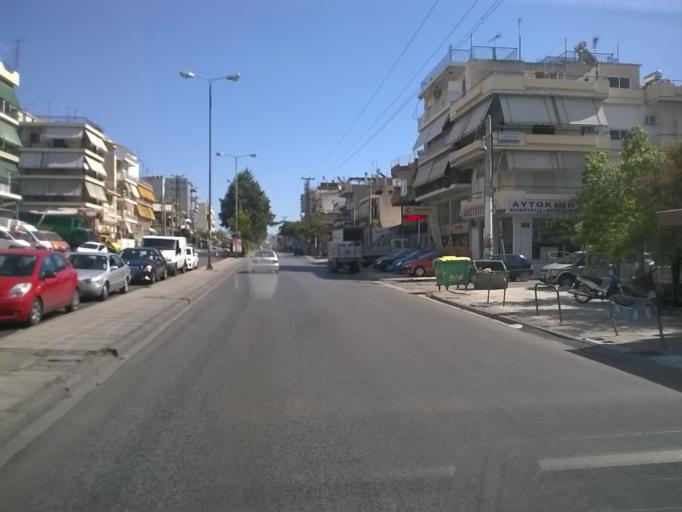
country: GR
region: Attica
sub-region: Nomos Piraios
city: Korydallos
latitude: 37.9779
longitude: 23.6317
